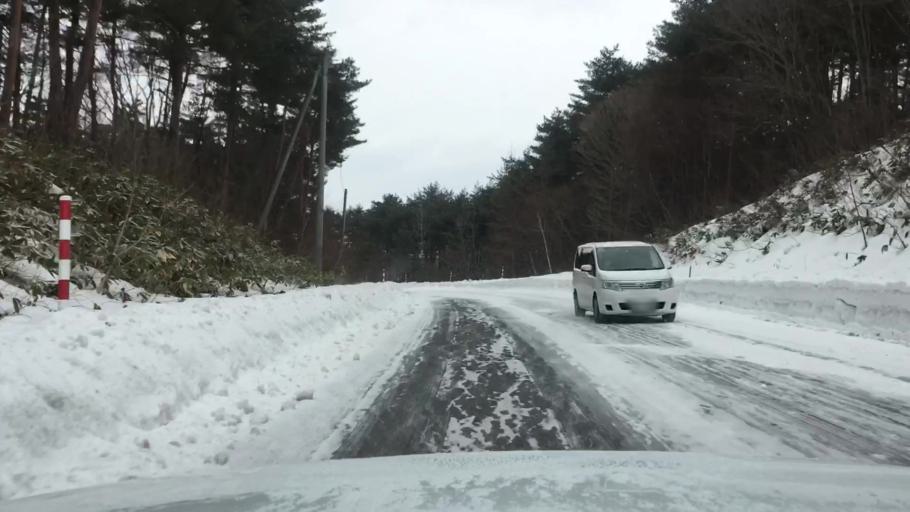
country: JP
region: Iwate
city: Shizukuishi
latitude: 39.9466
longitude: 140.9981
